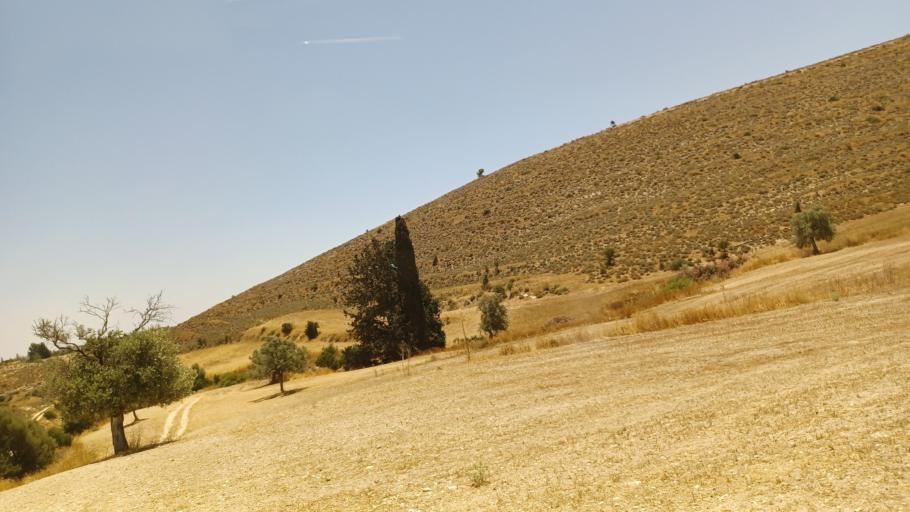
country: CY
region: Lefkosia
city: Lympia
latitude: 34.9919
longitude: 33.4906
